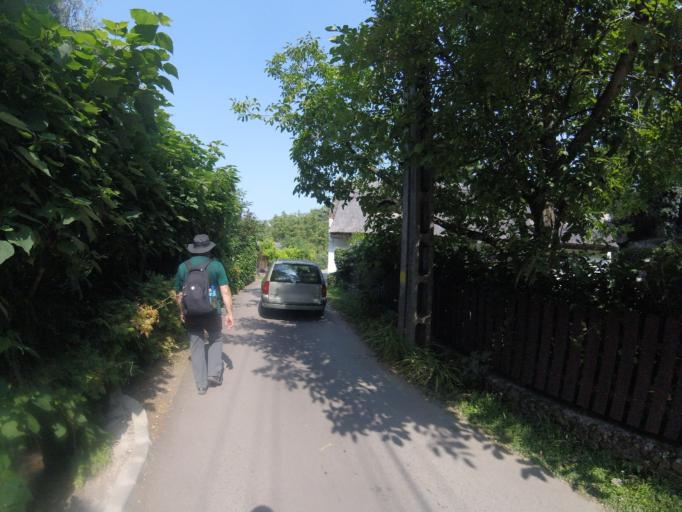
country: HU
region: Veszprem
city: Badacsonytomaj
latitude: 46.8023
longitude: 17.4354
